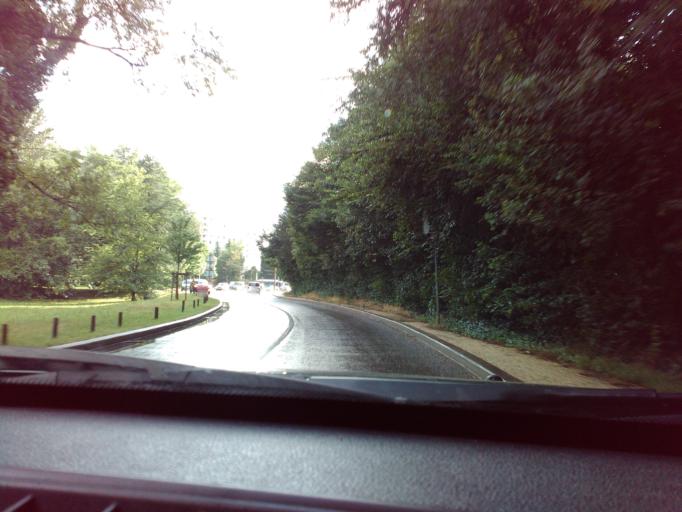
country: FR
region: Rhone-Alpes
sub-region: Departement de l'Isere
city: La Tronche
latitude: 45.1914
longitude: 5.7403
